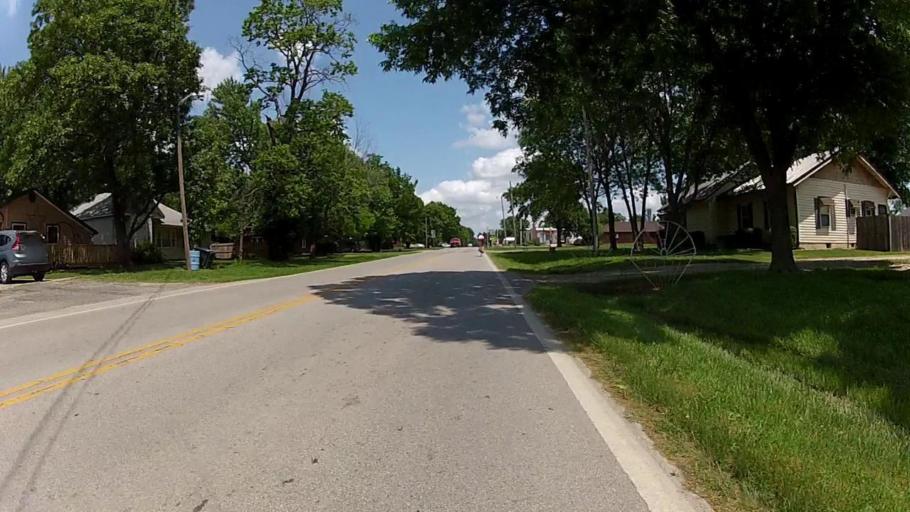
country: US
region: Kansas
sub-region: Labette County
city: Altamont
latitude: 37.1930
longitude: -95.2990
